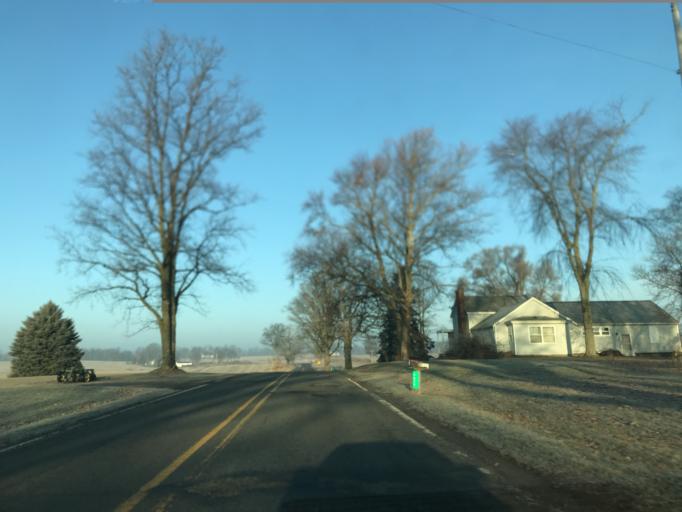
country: US
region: Michigan
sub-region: Ingham County
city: Leslie
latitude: 42.4195
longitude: -84.5135
